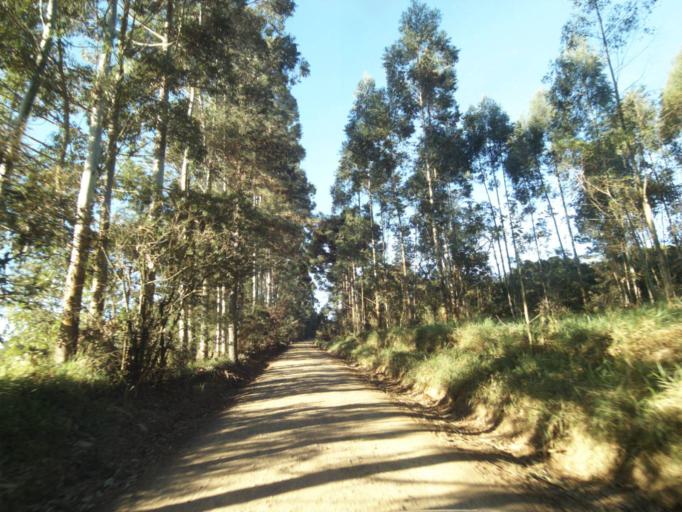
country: BR
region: Parana
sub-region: Tibagi
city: Tibagi
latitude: -24.5423
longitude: -50.6141
